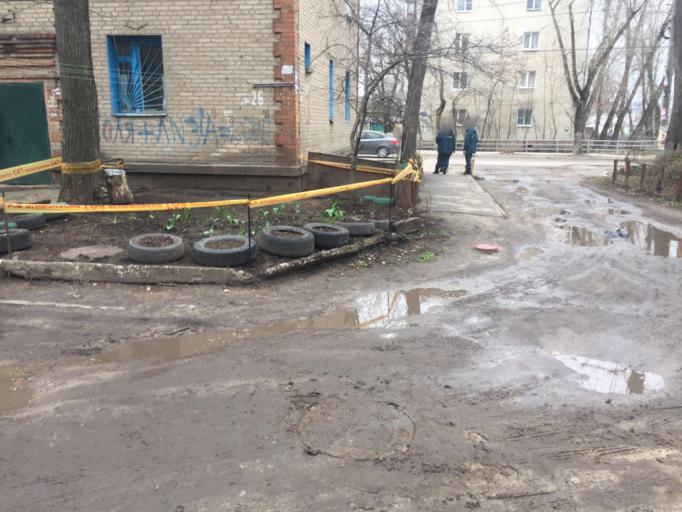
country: RU
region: Voronezj
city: Voronezh
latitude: 51.6768
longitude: 39.1535
